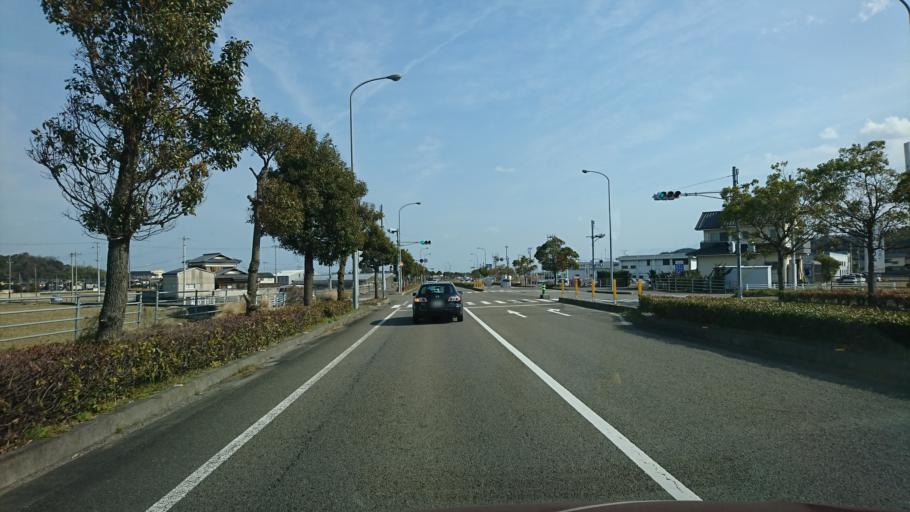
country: JP
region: Ehime
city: Saijo
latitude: 34.0194
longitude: 133.0234
